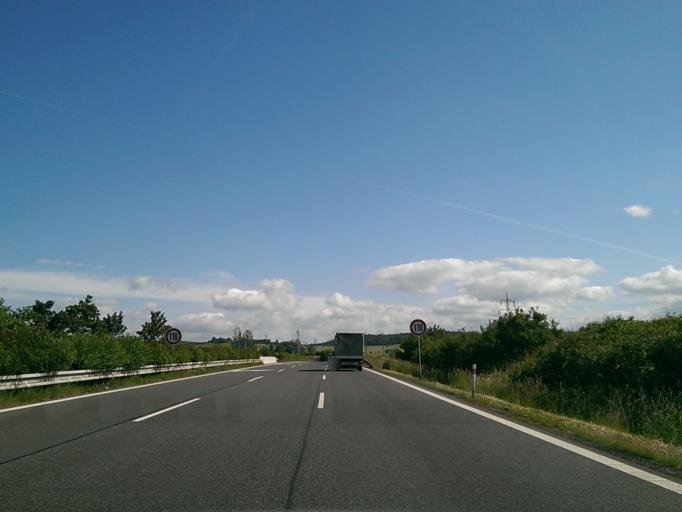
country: CZ
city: Ohrazenice
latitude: 50.6296
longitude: 15.1096
